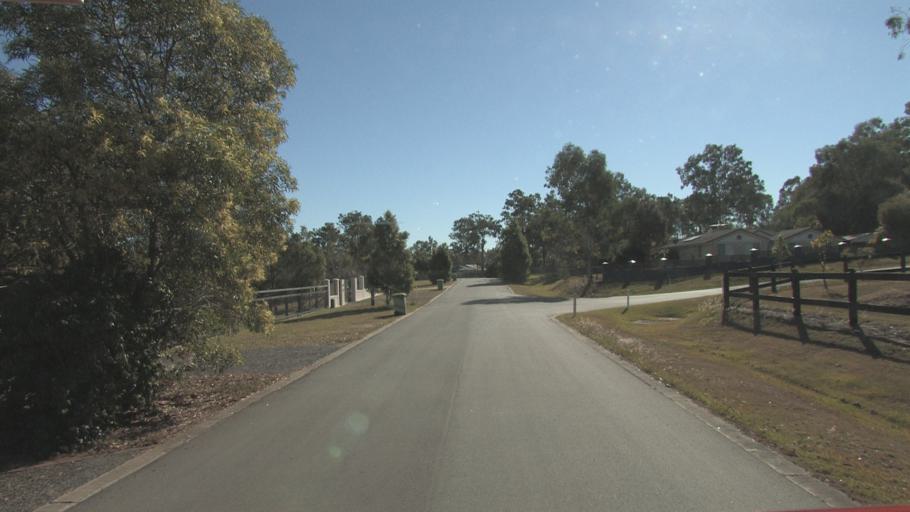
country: AU
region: Queensland
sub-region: Logan
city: North Maclean
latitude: -27.7343
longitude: 152.9681
